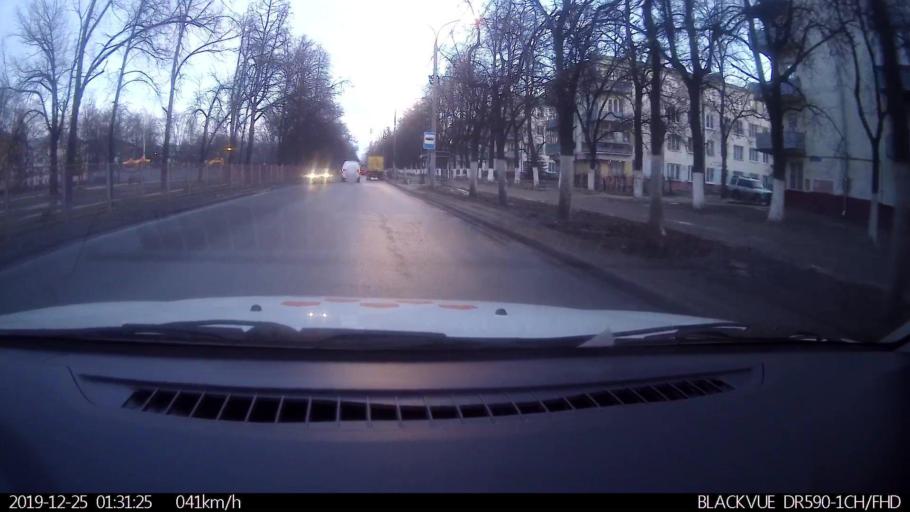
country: RU
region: Nizjnij Novgorod
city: Gorbatovka
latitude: 56.2455
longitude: 43.8575
